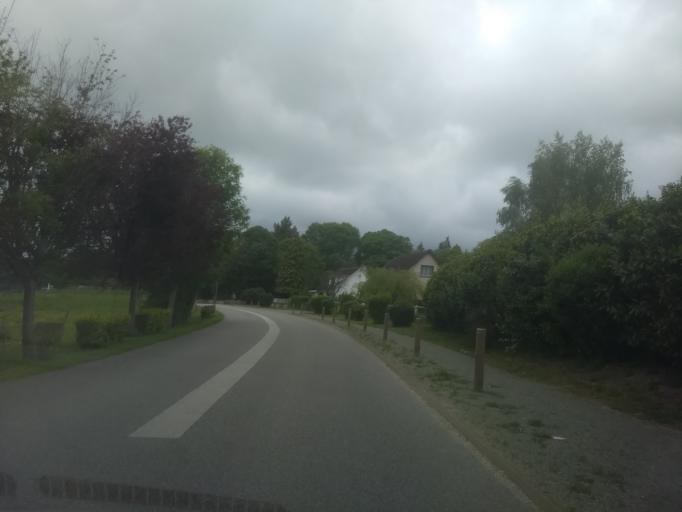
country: FR
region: Lower Normandy
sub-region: Departement de l'Orne
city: Bretoncelles
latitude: 48.4763
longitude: 0.8516
